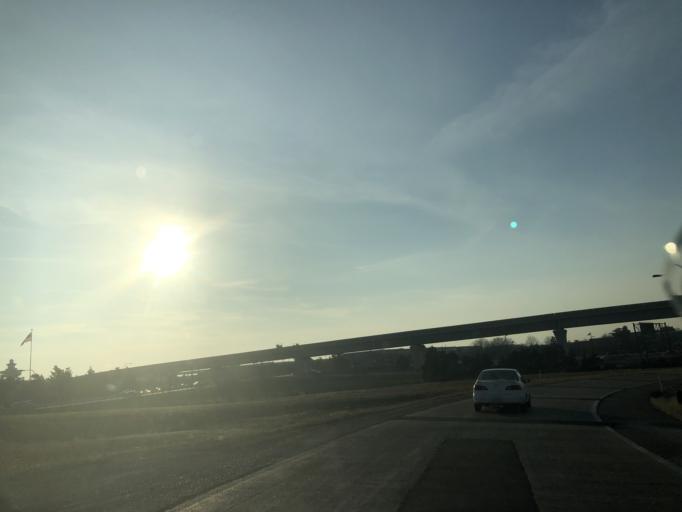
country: US
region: Virginia
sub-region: Fairfax County
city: Floris
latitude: 38.9593
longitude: -77.4417
